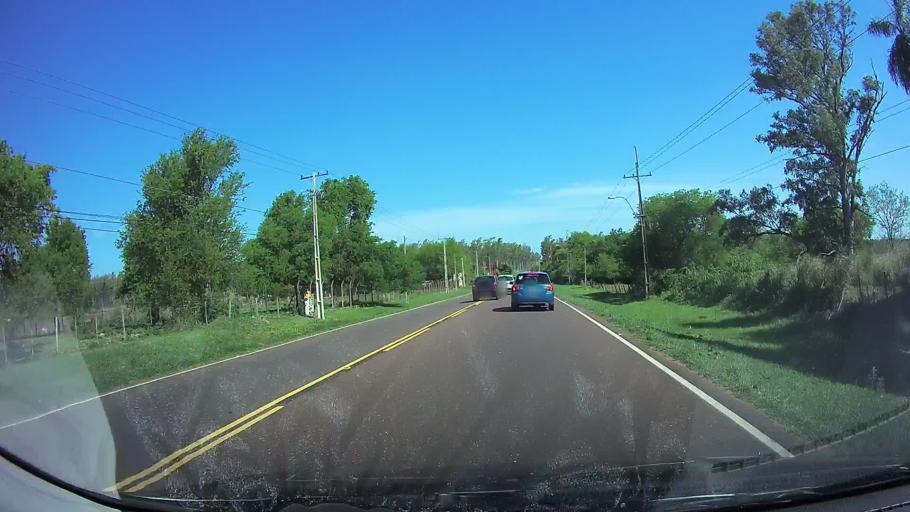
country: PY
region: Central
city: Ypacarai
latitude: -25.3700
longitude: -57.2636
